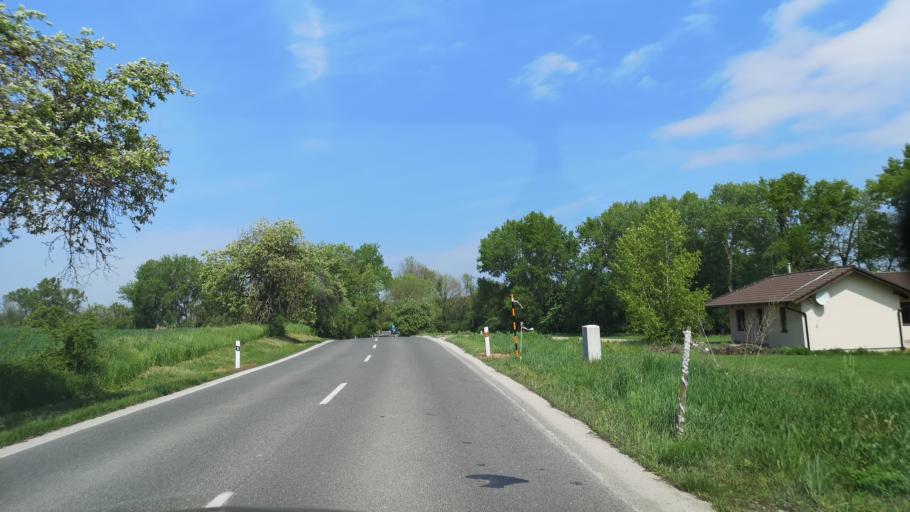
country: SK
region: Trnavsky
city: Vrbove
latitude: 48.5305
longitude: 17.6083
